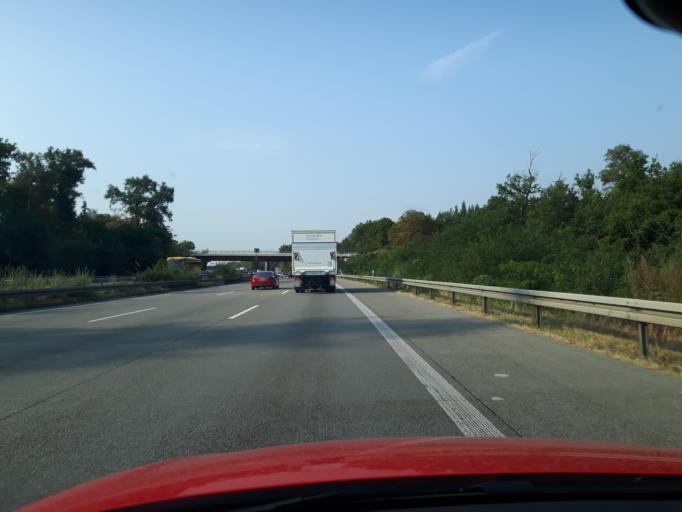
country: DE
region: Baden-Wuerttemberg
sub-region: Karlsruhe Region
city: Weingarten
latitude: 49.0751
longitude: 8.5127
